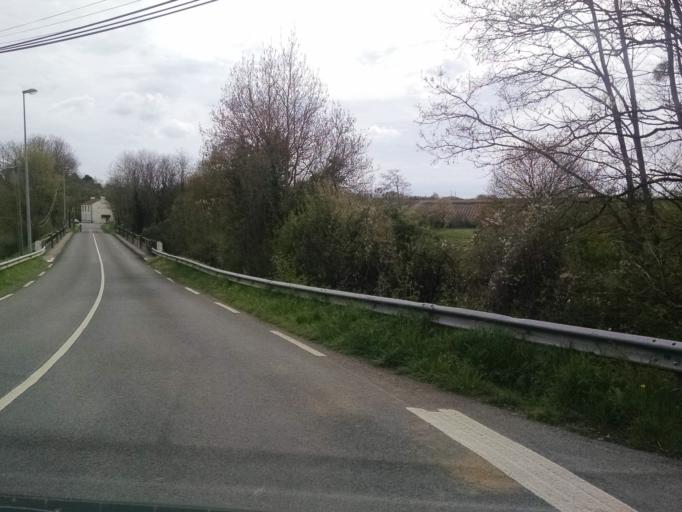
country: FR
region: Pays de la Loire
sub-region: Departement de la Loire-Atlantique
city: Gorges
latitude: 47.1076
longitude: -1.3041
